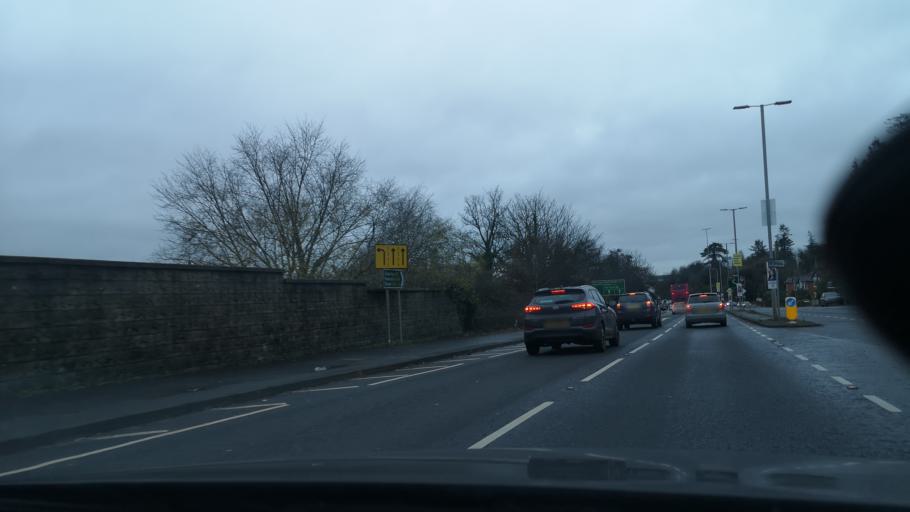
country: GB
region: Northern Ireland
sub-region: Castlereagh District
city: Castlereagh
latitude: 54.5597
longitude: -5.9126
